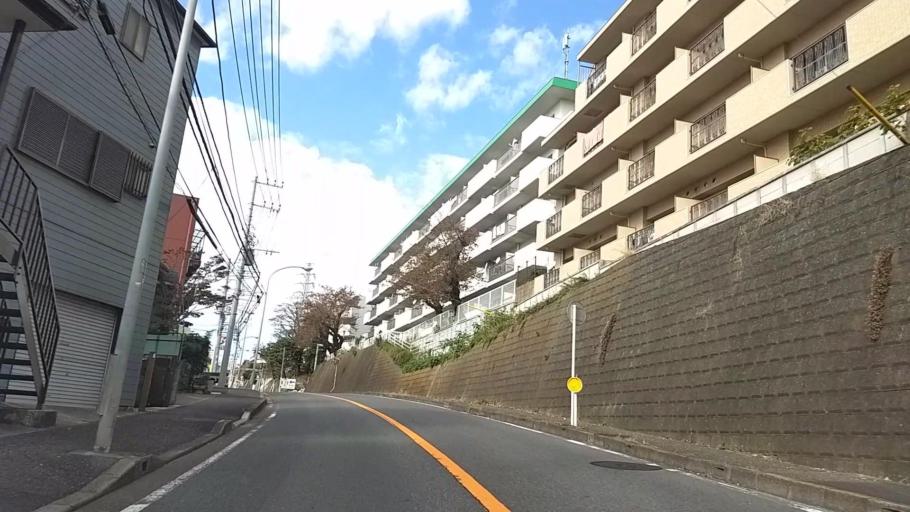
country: JP
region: Kanagawa
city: Yokohama
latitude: 35.4908
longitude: 139.6387
